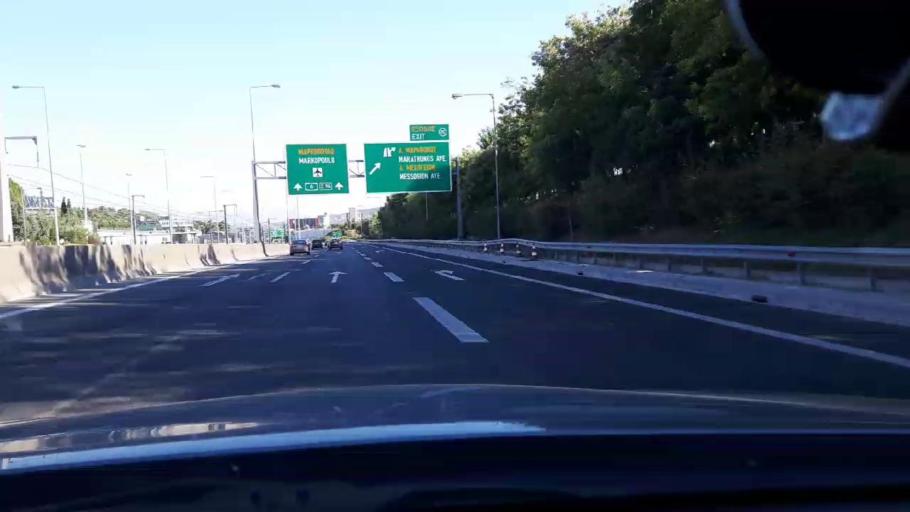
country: GR
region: Attica
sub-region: Nomarchia Anatolikis Attikis
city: Pallini
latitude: 37.9989
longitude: 23.8714
